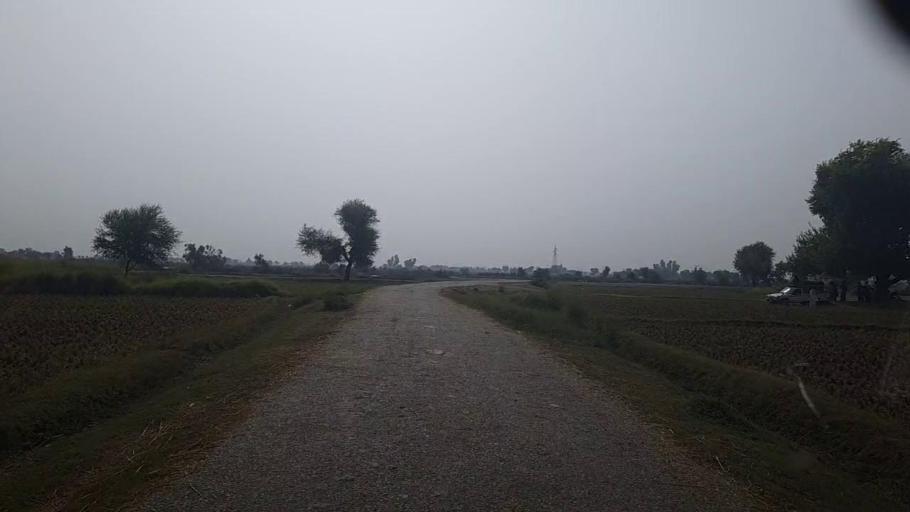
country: PK
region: Sindh
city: Kashmor
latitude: 28.3970
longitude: 69.4203
